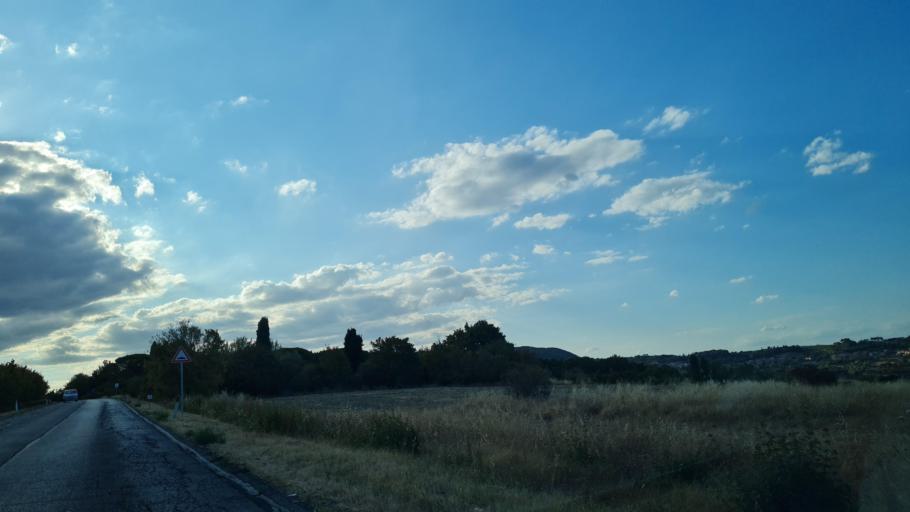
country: IT
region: Tuscany
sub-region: Provincia di Siena
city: Chianciano Terme
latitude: 43.0351
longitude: 11.8399
